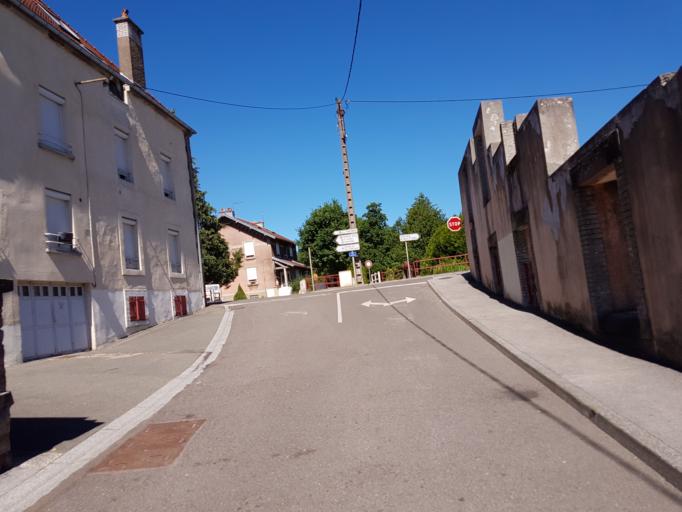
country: FR
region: Franche-Comte
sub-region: Departement de la Haute-Saone
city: Saint-Sauveur
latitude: 47.8151
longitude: 6.3833
